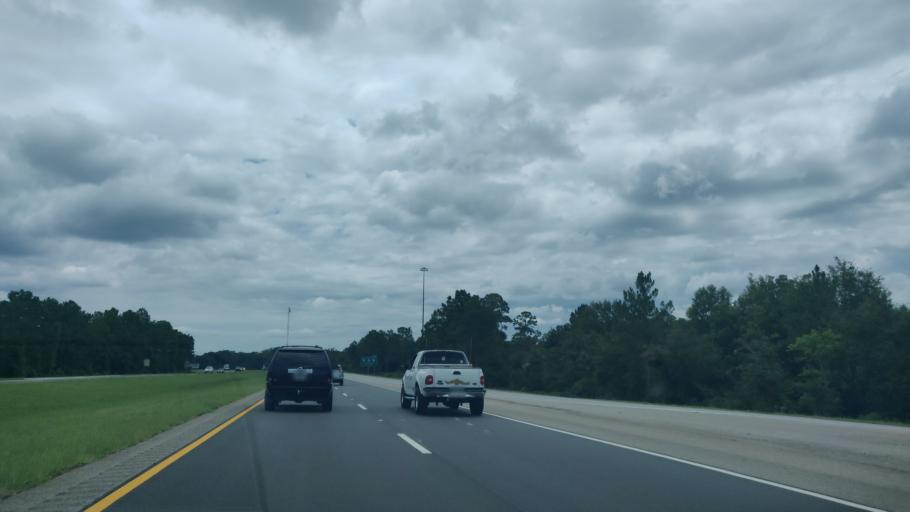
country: US
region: Georgia
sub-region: Dougherty County
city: Albany
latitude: 31.6162
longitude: -84.2006
